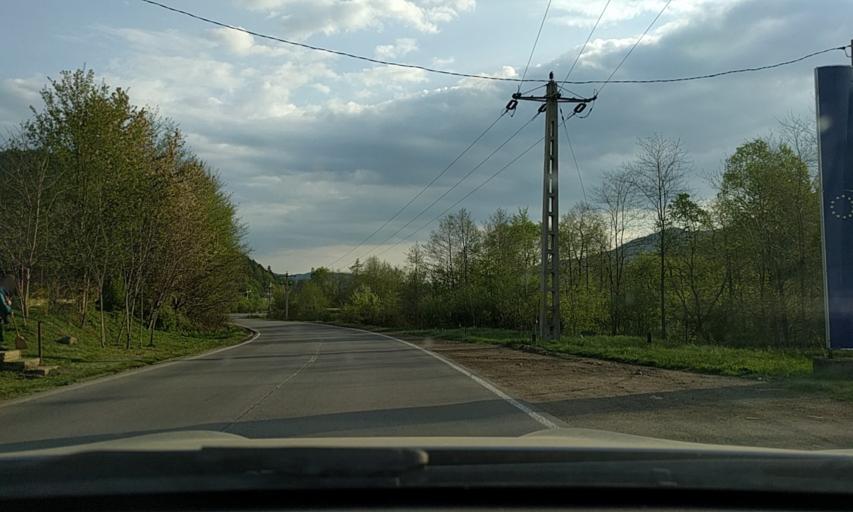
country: RO
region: Bacau
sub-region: Oras Slanic-Moldova
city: Slanic-Moldova
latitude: 46.1335
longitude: 26.4480
